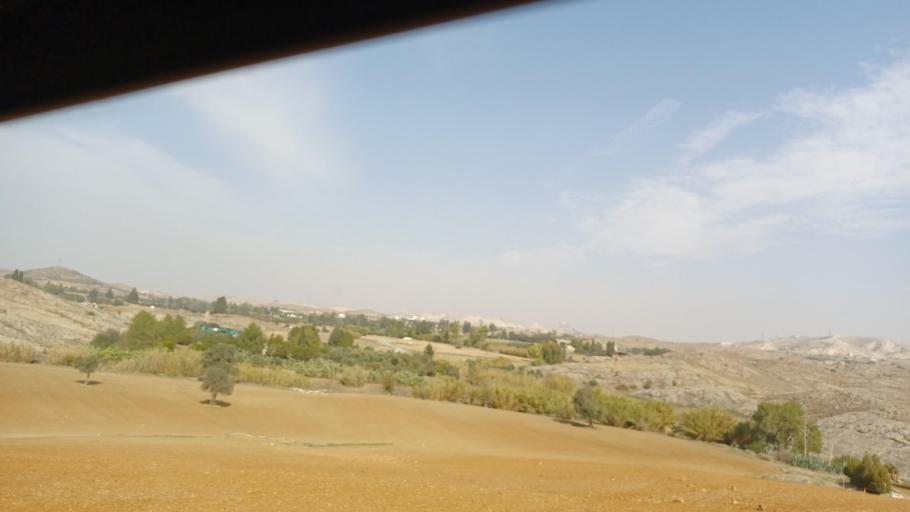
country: CY
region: Larnaka
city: Mosfiloti
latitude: 34.9646
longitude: 33.4430
